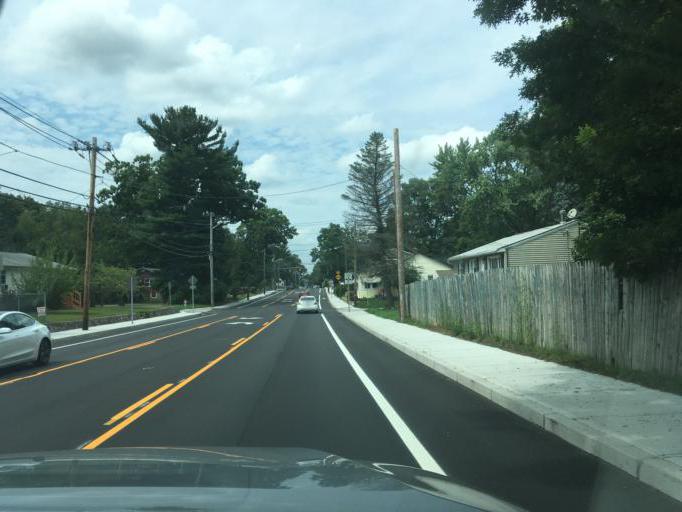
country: US
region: Rhode Island
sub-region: Kent County
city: West Warwick
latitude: 41.6727
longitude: -71.5539
